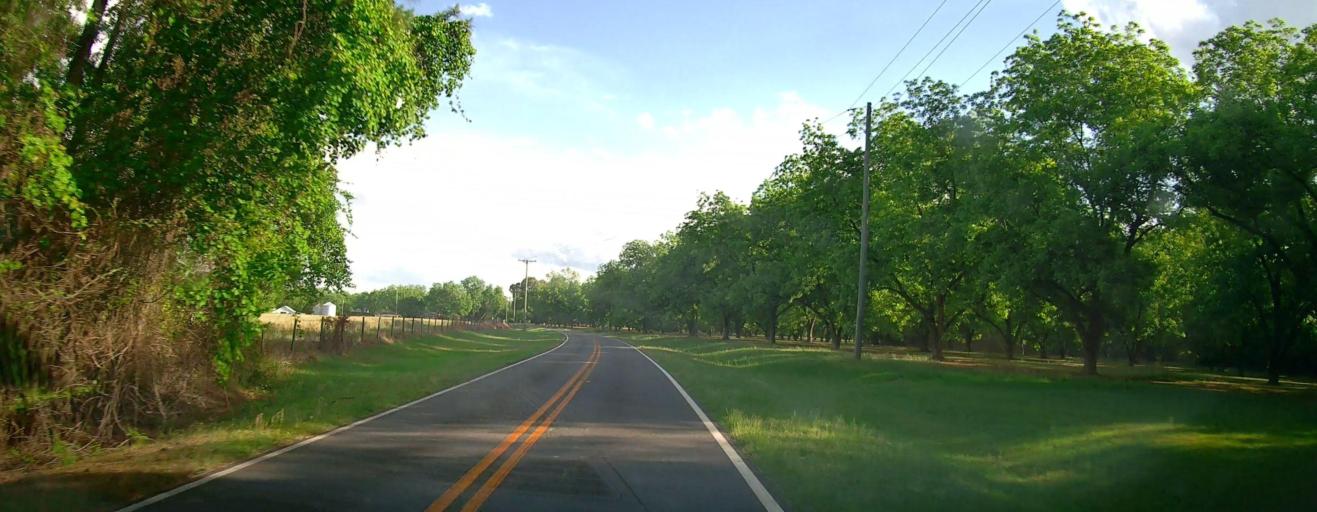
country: US
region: Georgia
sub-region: Peach County
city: Byron
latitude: 32.6694
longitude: -83.8019
